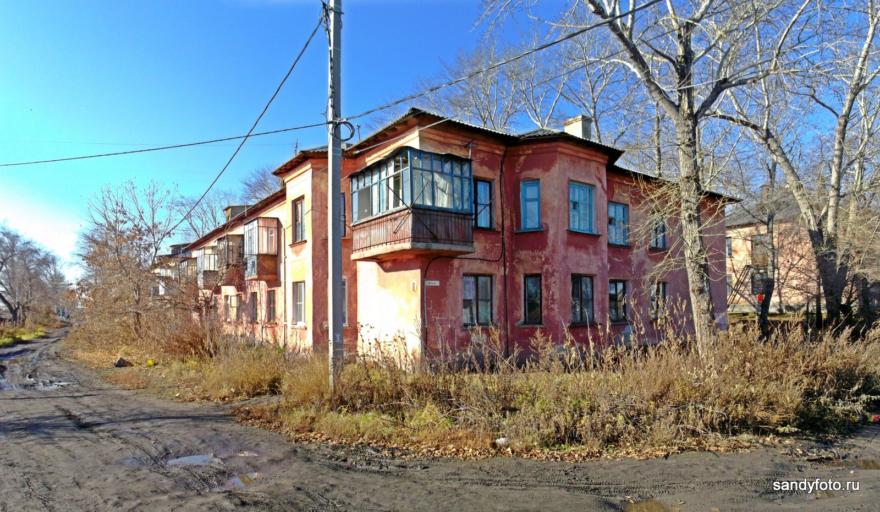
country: RU
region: Chelyabinsk
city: Troitsk
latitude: 54.1099
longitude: 61.5618
